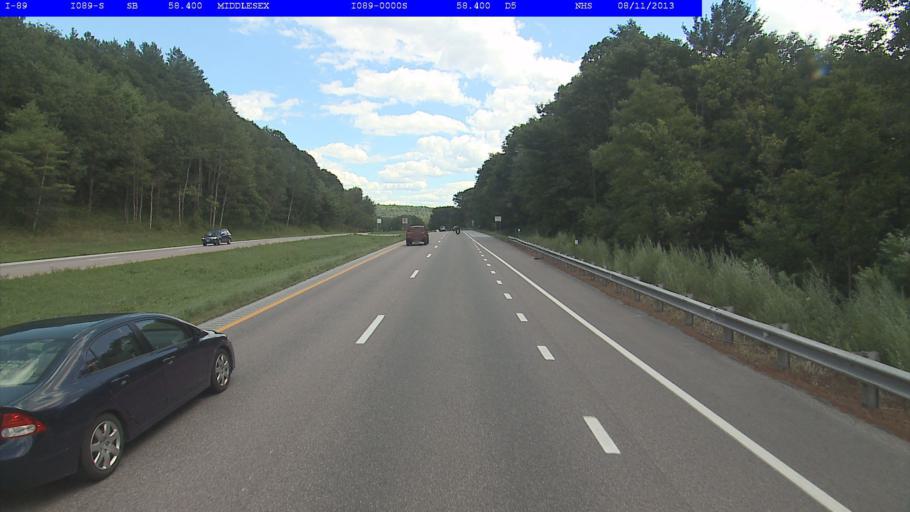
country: US
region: Vermont
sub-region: Washington County
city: Waterbury
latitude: 44.2952
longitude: -72.6804
